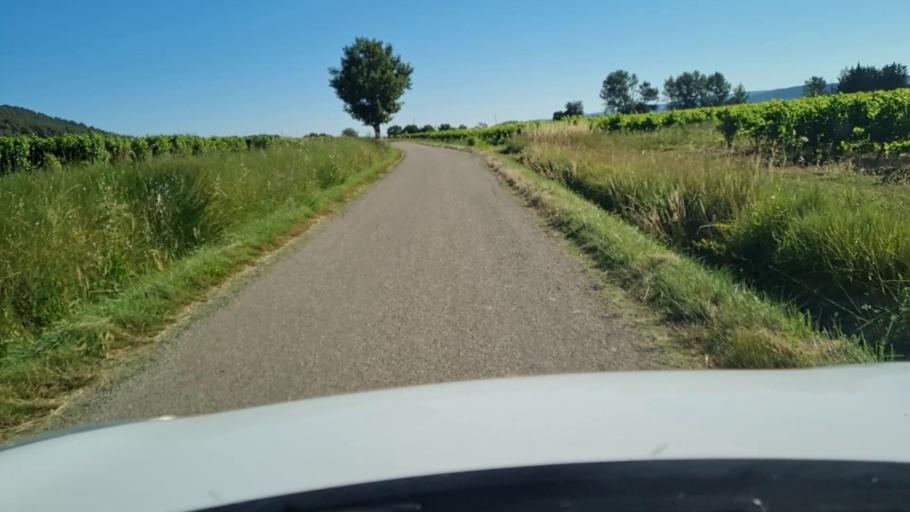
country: FR
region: Languedoc-Roussillon
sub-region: Departement du Gard
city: Sommieres
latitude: 43.8348
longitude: 4.0299
